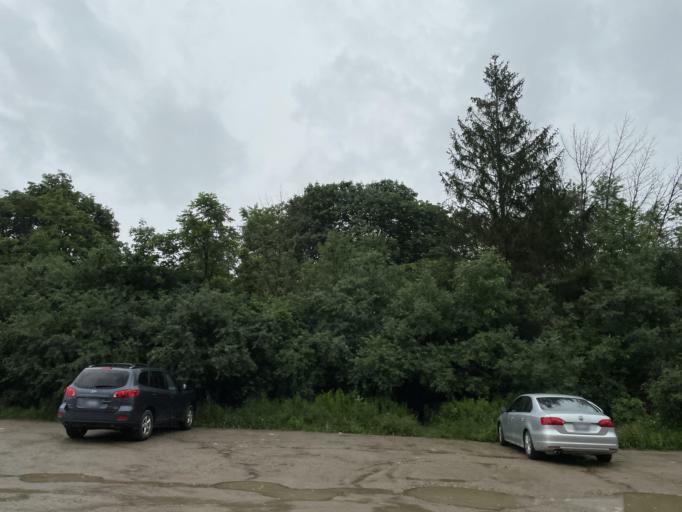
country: CA
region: Ontario
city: Cambridge
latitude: 43.4276
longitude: -80.2592
